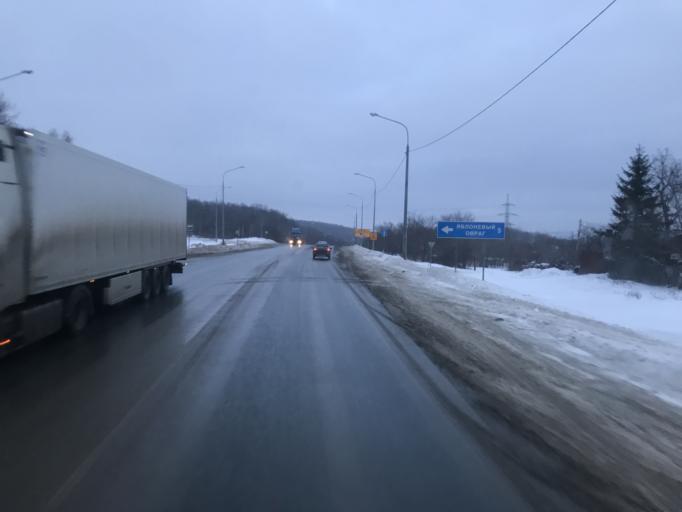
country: RU
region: Samara
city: Zhigulevsk
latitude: 53.3858
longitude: 49.4559
